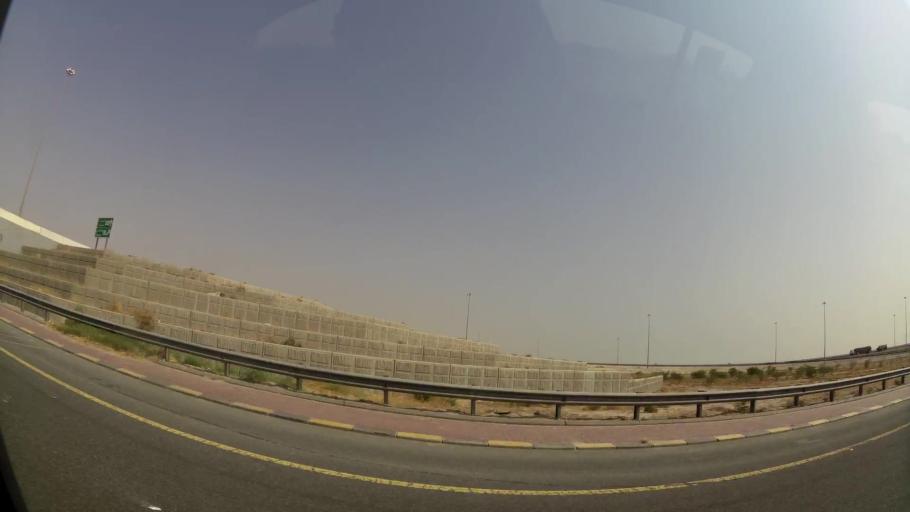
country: KW
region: Muhafazat al Jahra'
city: Al Jahra'
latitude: 29.3734
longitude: 47.6621
